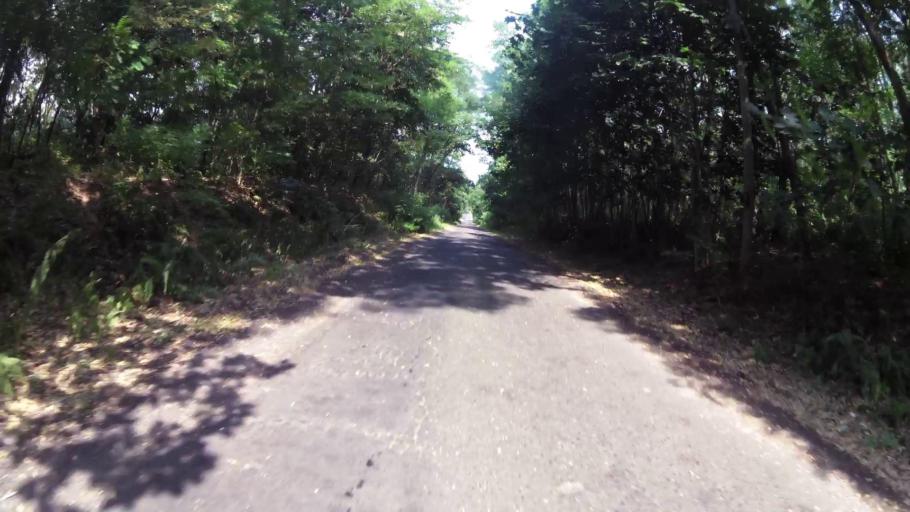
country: PL
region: West Pomeranian Voivodeship
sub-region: Powiat gryfinski
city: Mieszkowice
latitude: 52.8544
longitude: 14.5253
